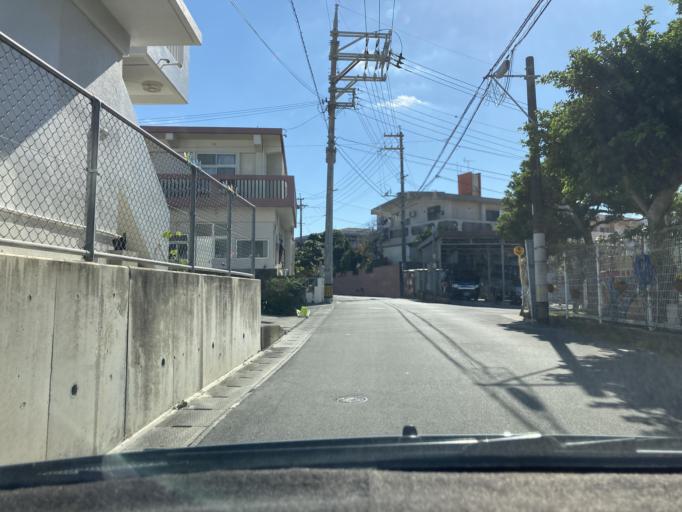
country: JP
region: Okinawa
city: Okinawa
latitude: 26.3462
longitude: 127.8290
